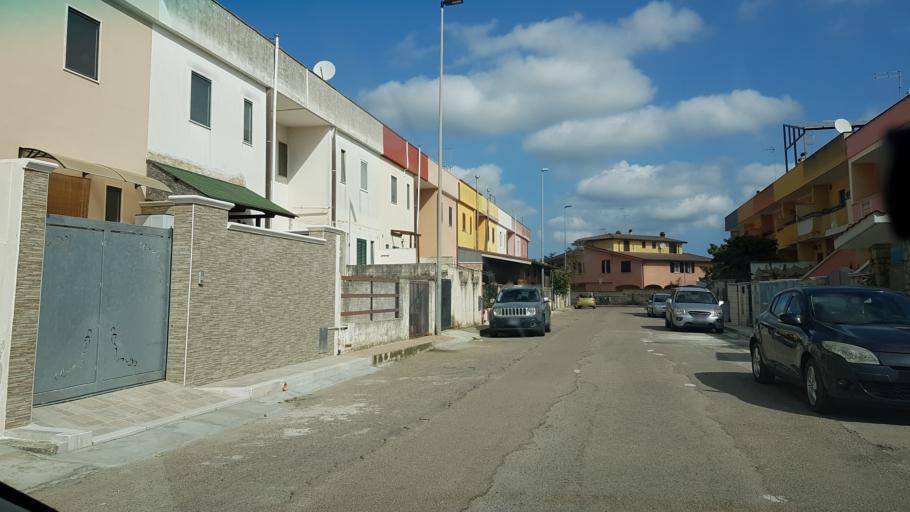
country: IT
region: Apulia
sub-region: Provincia di Brindisi
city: San Pietro Vernotico
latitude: 40.4780
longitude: 17.9998
